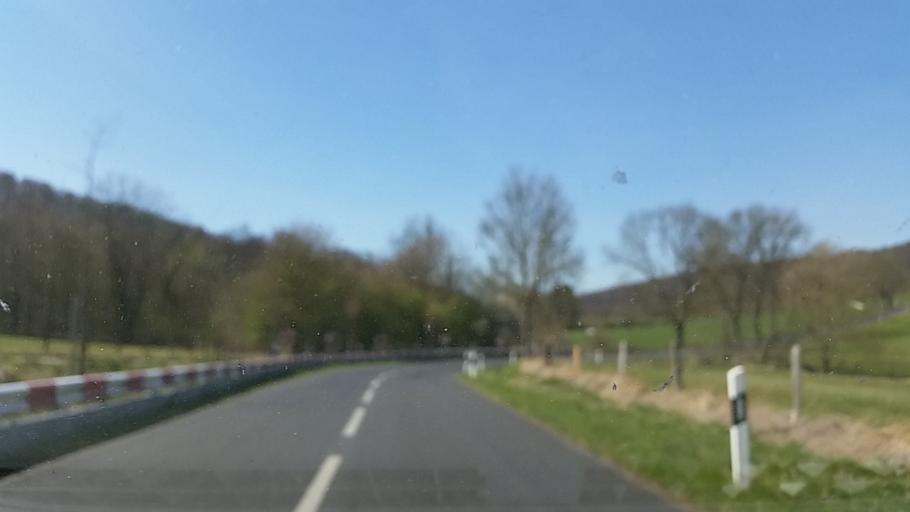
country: DE
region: Lower Saxony
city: Kneitlingen
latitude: 52.2072
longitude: 10.7500
